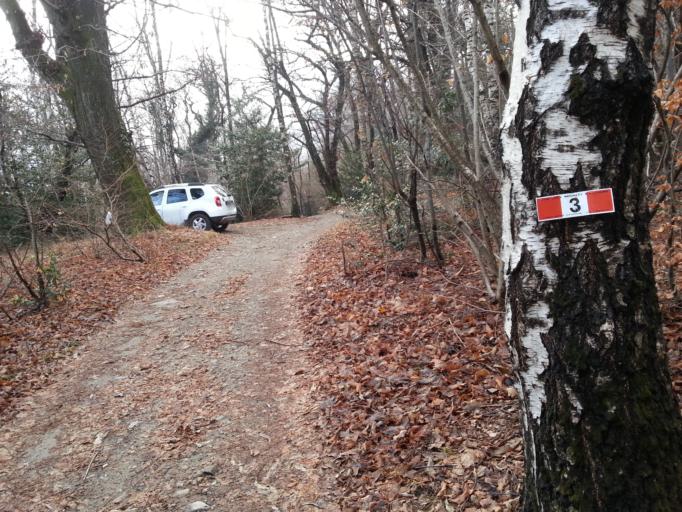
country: IT
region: Lombardy
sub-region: Provincia di Como
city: Plesio
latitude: 46.0478
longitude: 9.2218
